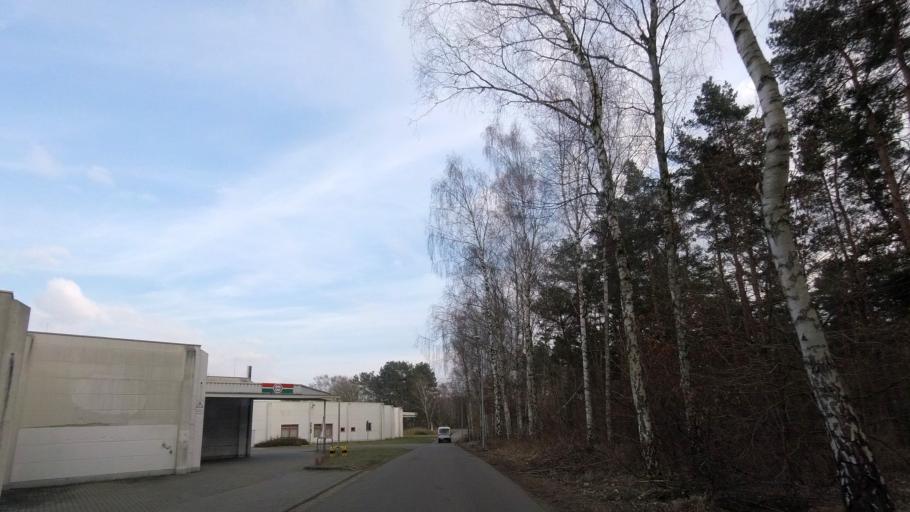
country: DE
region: Brandenburg
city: Belzig
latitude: 52.1433
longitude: 12.6116
